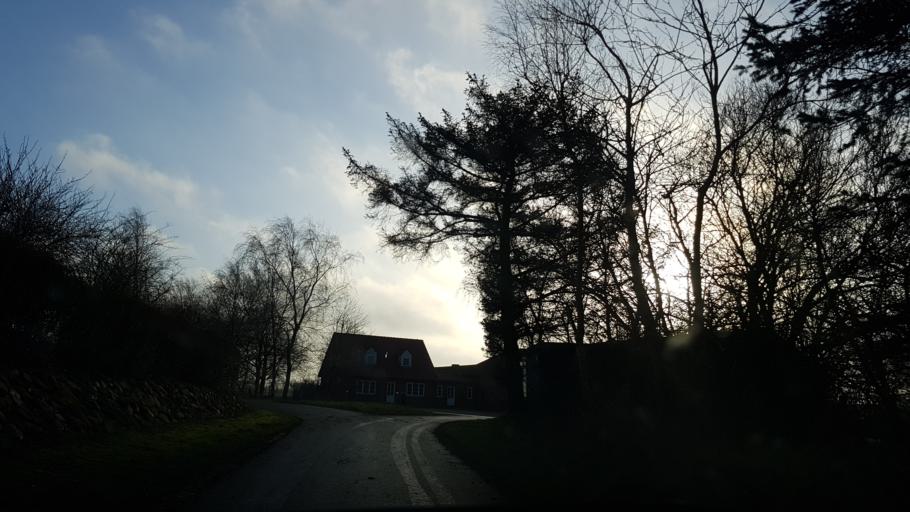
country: DK
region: South Denmark
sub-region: Aabenraa Kommune
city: Rodekro
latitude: 55.1561
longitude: 9.3086
